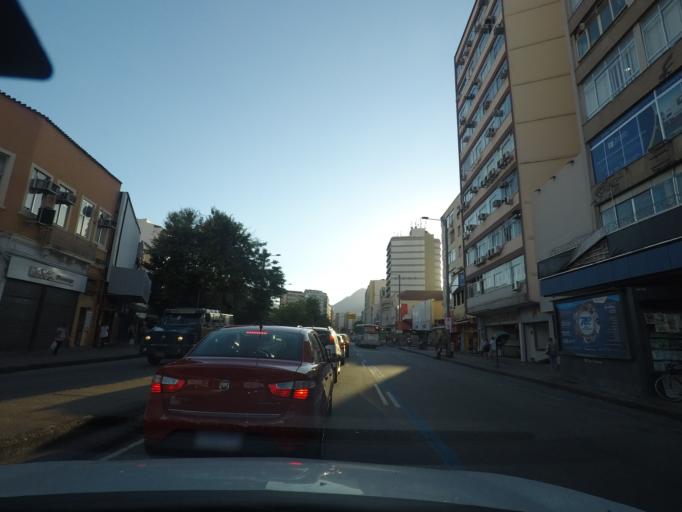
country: BR
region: Rio de Janeiro
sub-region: Rio De Janeiro
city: Rio de Janeiro
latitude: -22.9232
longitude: -43.2314
